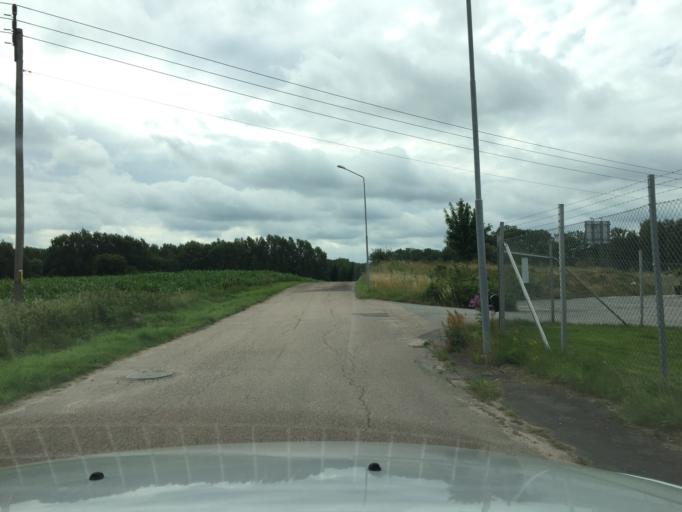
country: SE
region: Skane
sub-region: Hassleholms Kommun
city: Sosdala
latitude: 56.0376
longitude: 13.6901
